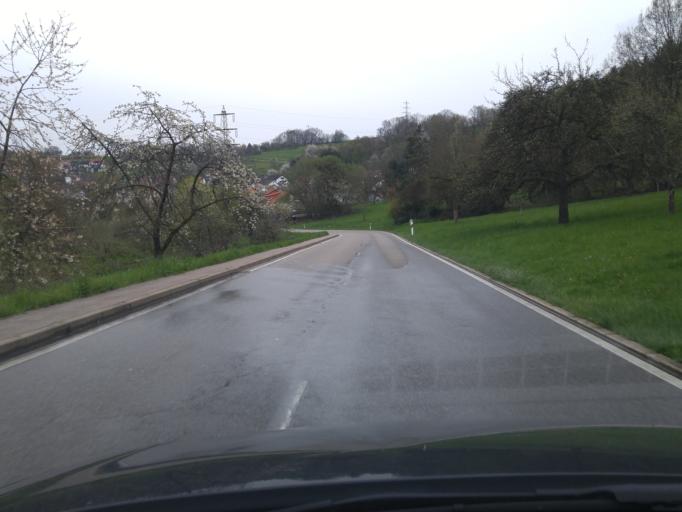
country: DE
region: Hesse
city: Neckarsteinach
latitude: 49.3906
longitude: 8.8509
